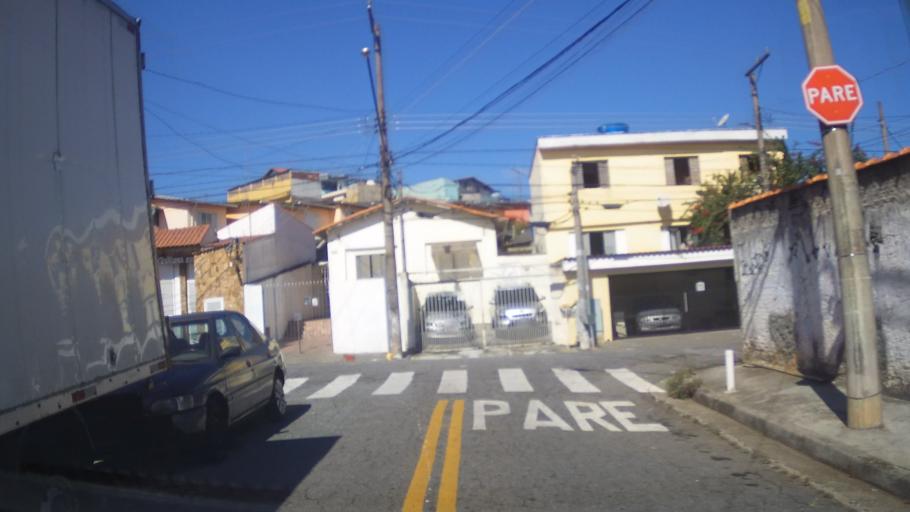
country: BR
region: Sao Paulo
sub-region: Sao Caetano Do Sul
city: Sao Caetano do Sul
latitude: -23.6481
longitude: -46.5654
